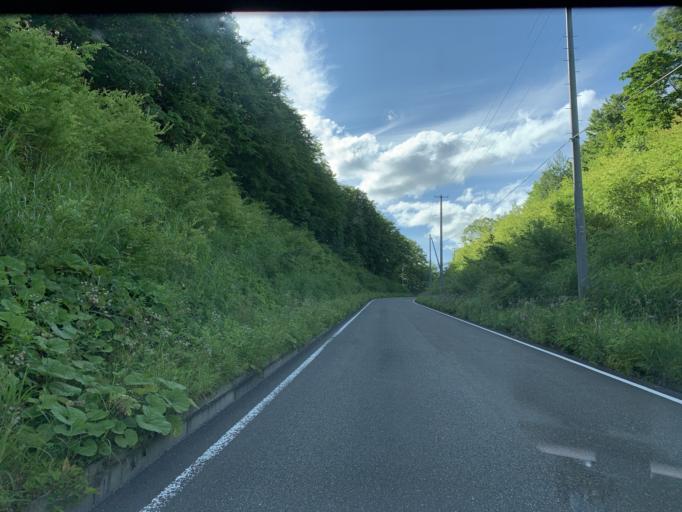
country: JP
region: Iwate
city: Ichinoseki
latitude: 38.9084
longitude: 140.8324
